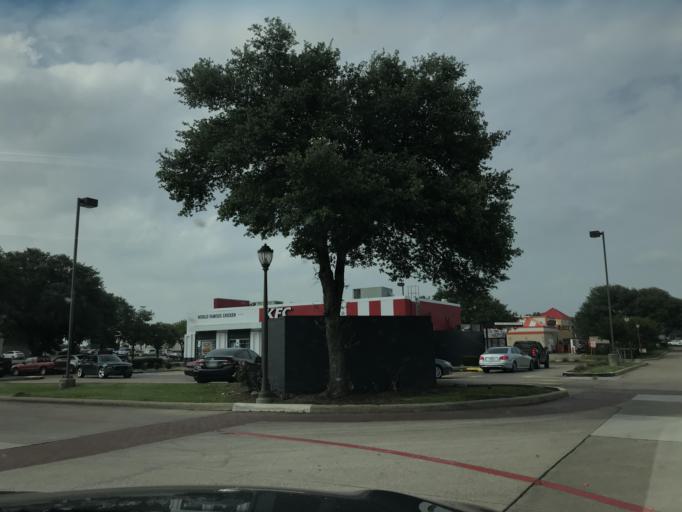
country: US
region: Texas
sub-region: Tarrant County
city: Benbrook
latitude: 32.6598
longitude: -97.4029
